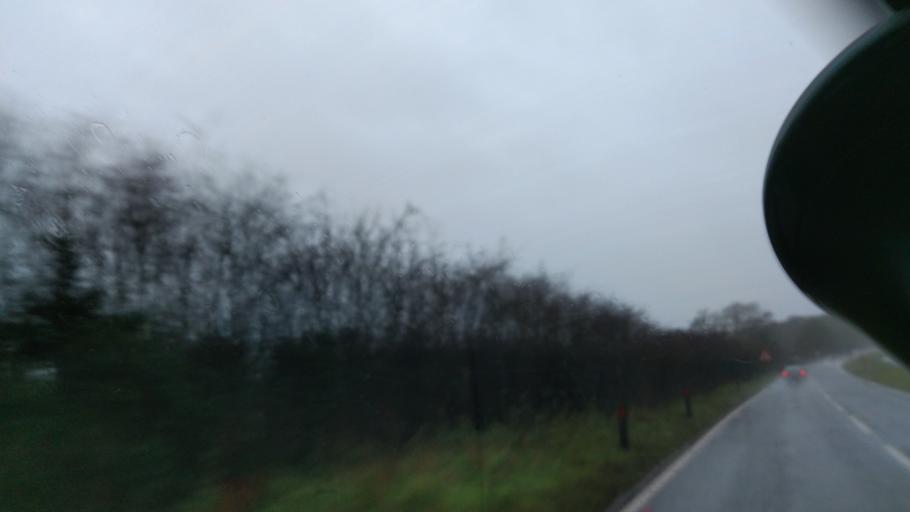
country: GB
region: England
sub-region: West Sussex
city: Goring-by-Sea
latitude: 50.8399
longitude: -0.4273
